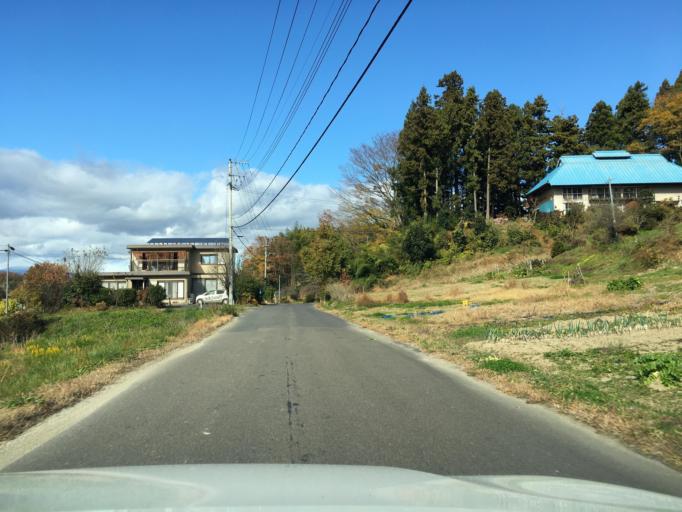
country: JP
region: Fukushima
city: Miharu
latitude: 37.5035
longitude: 140.4958
